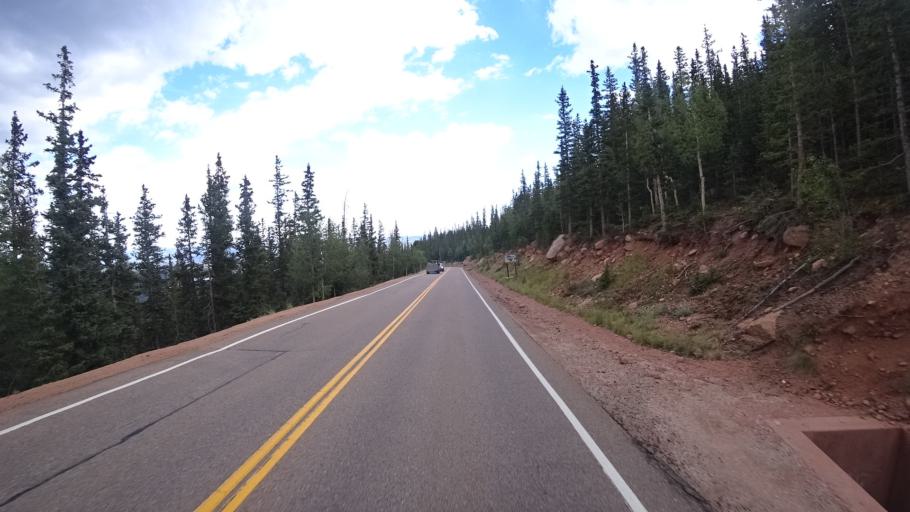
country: US
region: Colorado
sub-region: El Paso County
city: Cascade-Chipita Park
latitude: 38.8889
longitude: -105.0708
